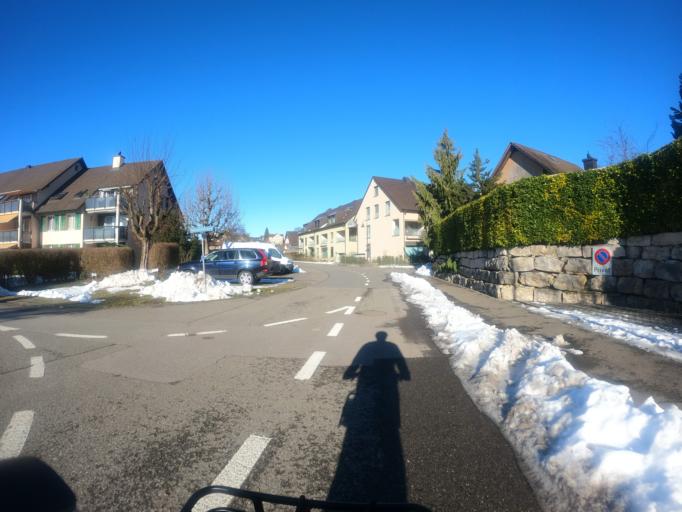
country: CH
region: Aargau
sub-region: Bezirk Bremgarten
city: Jonen
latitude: 47.2943
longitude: 8.3938
